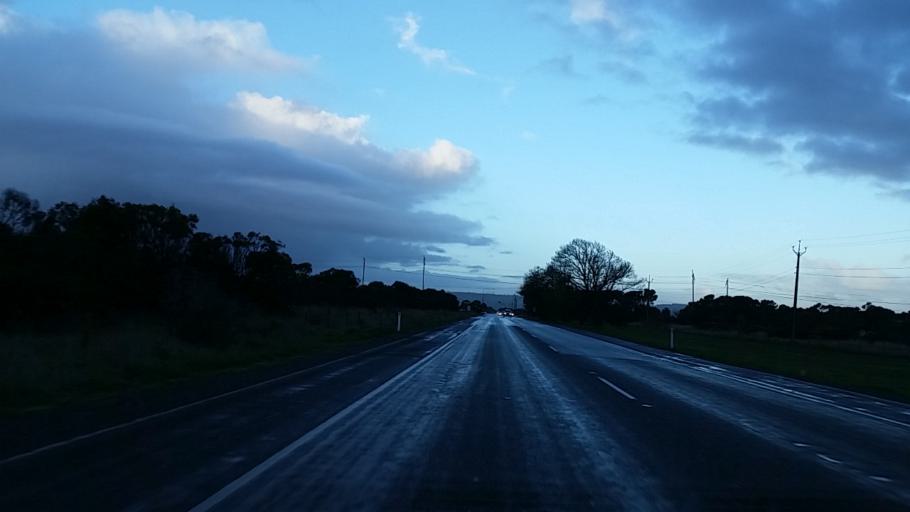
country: AU
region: South Australia
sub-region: Marion
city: Trott Park
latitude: -35.0547
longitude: 138.5405
